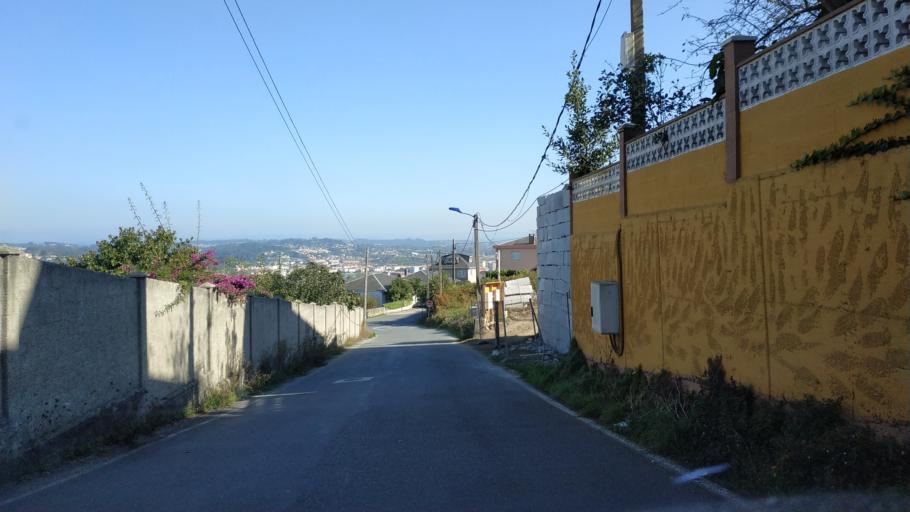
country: ES
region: Galicia
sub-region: Provincia da Coruna
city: Culleredo
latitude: 43.3244
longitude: -8.3883
